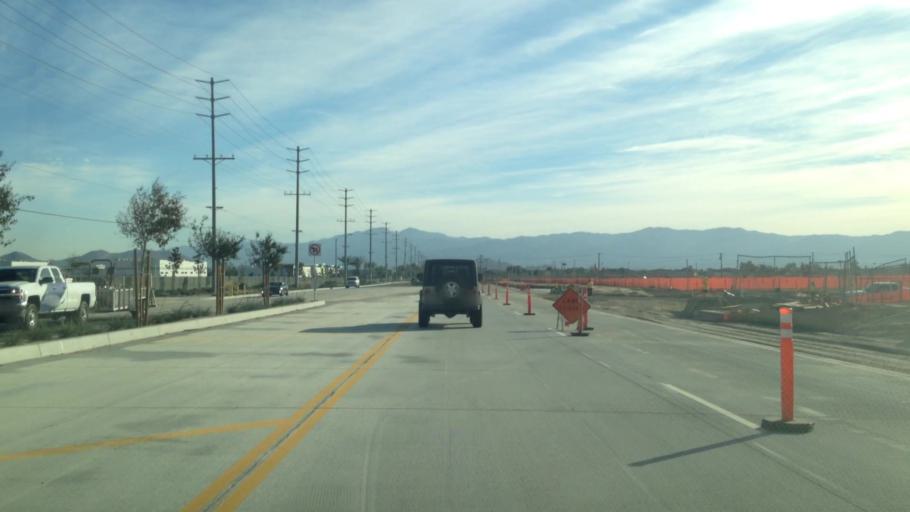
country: US
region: California
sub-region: Riverside County
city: Mira Loma
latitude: 33.9940
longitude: -117.5585
